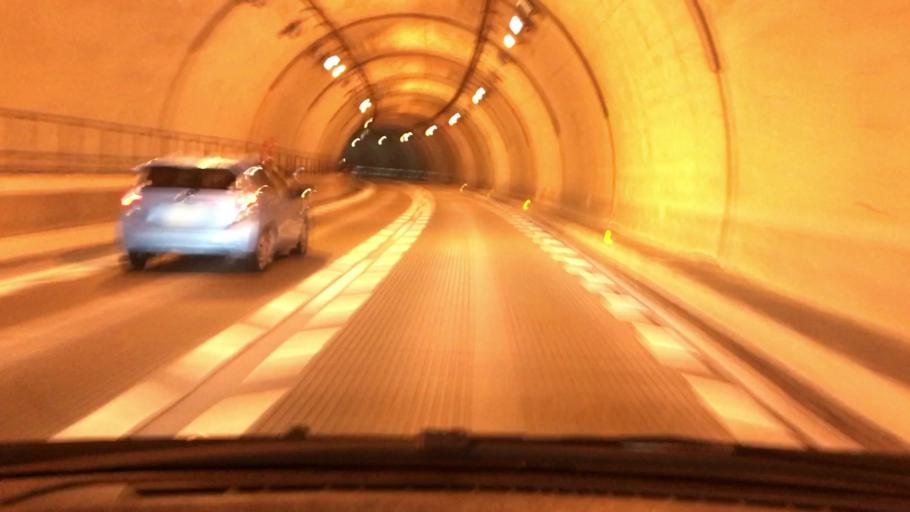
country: JP
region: Hyogo
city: Sandacho
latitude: 34.8197
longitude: 135.2581
